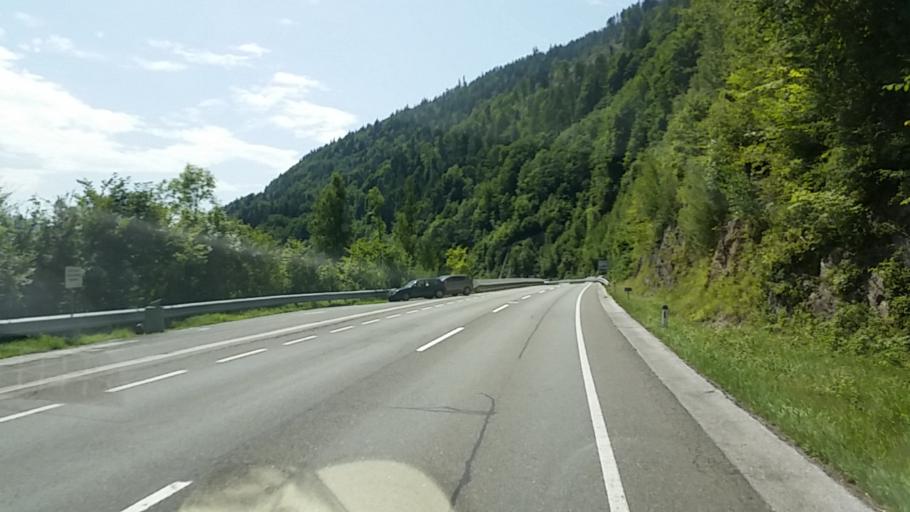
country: AT
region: Salzburg
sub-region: Politischer Bezirk Sankt Johann im Pongau
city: Pfarrwerfen
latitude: 47.4403
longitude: 13.2088
